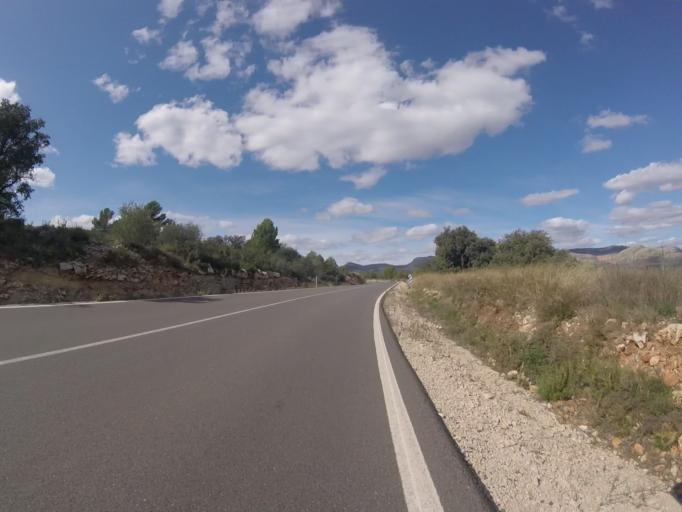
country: ES
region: Valencia
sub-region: Provincia de Castello
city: Chert/Xert
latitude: 40.4387
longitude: 0.1132
